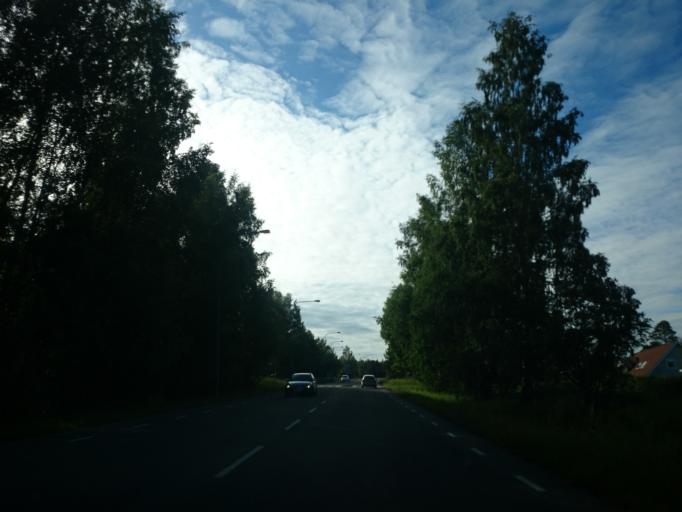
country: SE
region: Vaesternorrland
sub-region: Sundsvalls Kommun
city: Sundsvall
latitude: 62.4024
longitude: 17.3224
